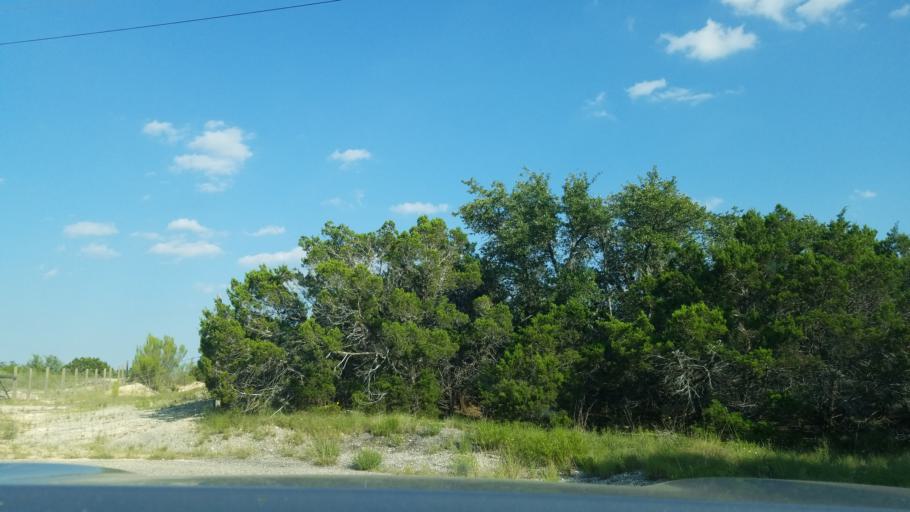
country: US
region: Texas
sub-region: Comal County
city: Bulverde
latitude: 29.7772
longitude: -98.4293
